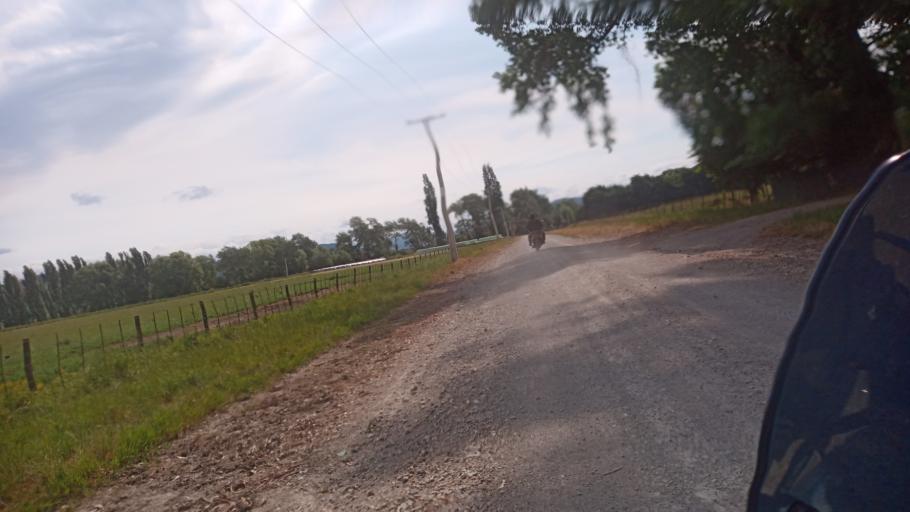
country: NZ
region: Gisborne
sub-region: Gisborne District
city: Gisborne
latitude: -38.4674
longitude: 177.8490
